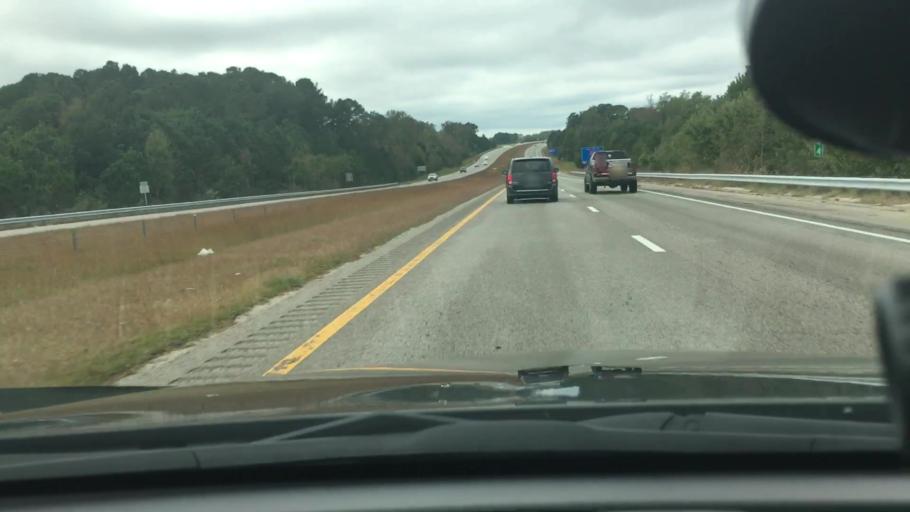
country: US
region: North Carolina
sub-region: Wilson County
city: Wilson
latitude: 35.6764
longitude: -77.9390
